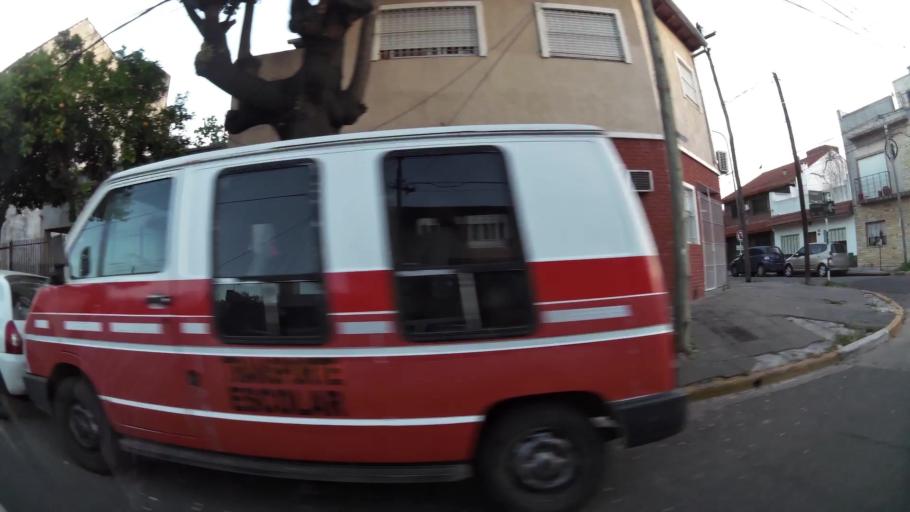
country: AR
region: Buenos Aires
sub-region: Partido de Vicente Lopez
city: Olivos
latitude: -34.5293
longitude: -58.5089
